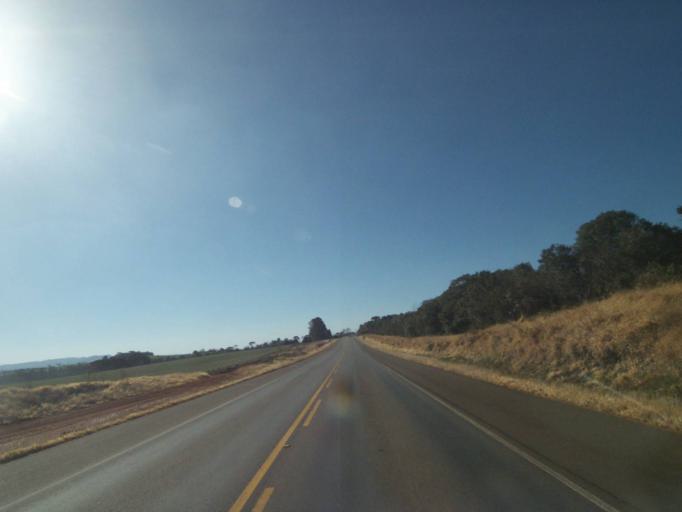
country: BR
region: Parana
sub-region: Tibagi
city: Tibagi
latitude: -24.7028
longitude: -50.4478
